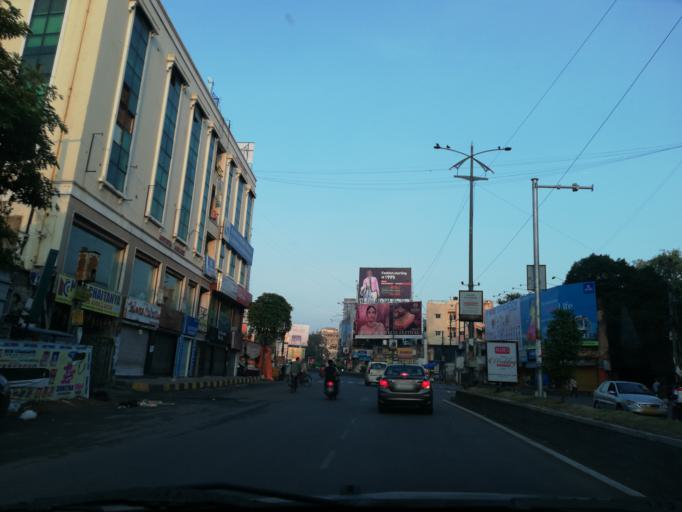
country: IN
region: Telangana
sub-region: Hyderabad
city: Hyderabad
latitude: 17.4006
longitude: 78.4892
